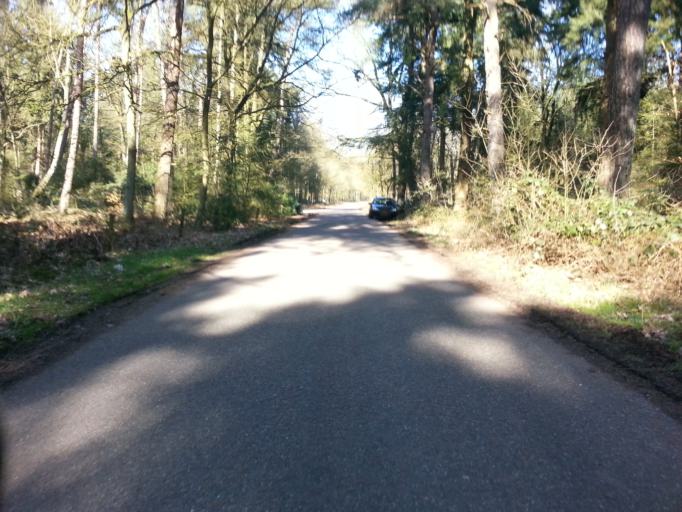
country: NL
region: Utrecht
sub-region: Gemeente Utrechtse Heuvelrug
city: Leersum
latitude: 52.0183
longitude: 5.3901
